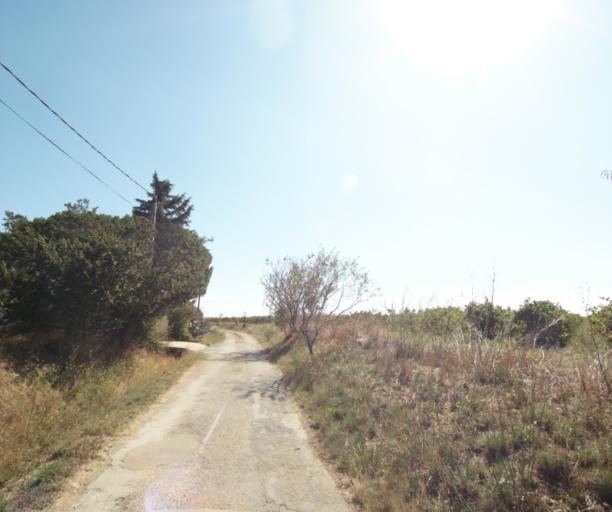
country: FR
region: Languedoc-Roussillon
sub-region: Departement du Gard
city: Rodilhan
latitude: 43.8201
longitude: 4.4334
